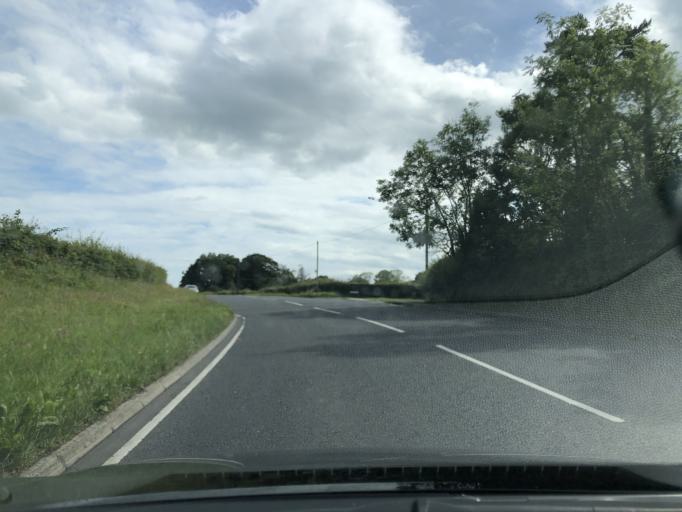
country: GB
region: Northern Ireland
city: Ballynahinch
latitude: 54.3894
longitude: -5.8832
